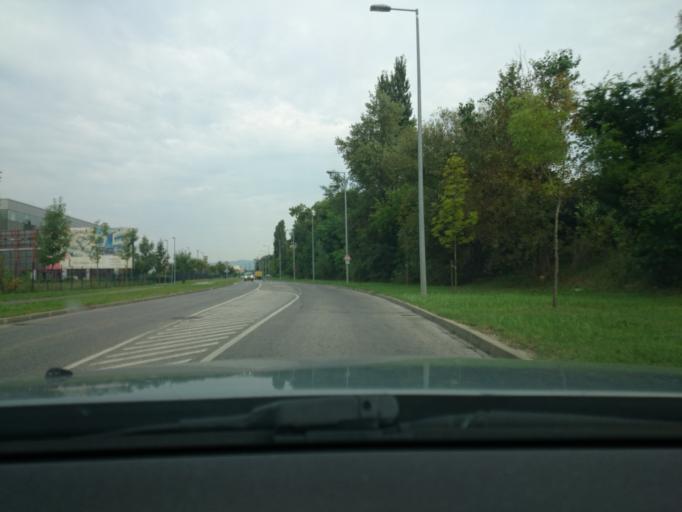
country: HU
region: Budapest
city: Budapest XX. keruelet
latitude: 47.4625
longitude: 19.0904
